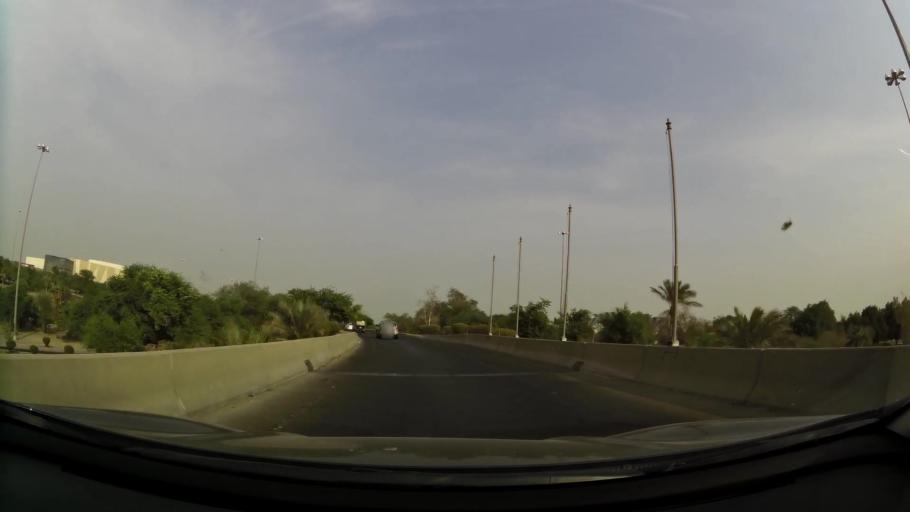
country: KW
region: Al Farwaniyah
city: Janub as Surrah
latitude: 29.2637
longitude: 47.9885
